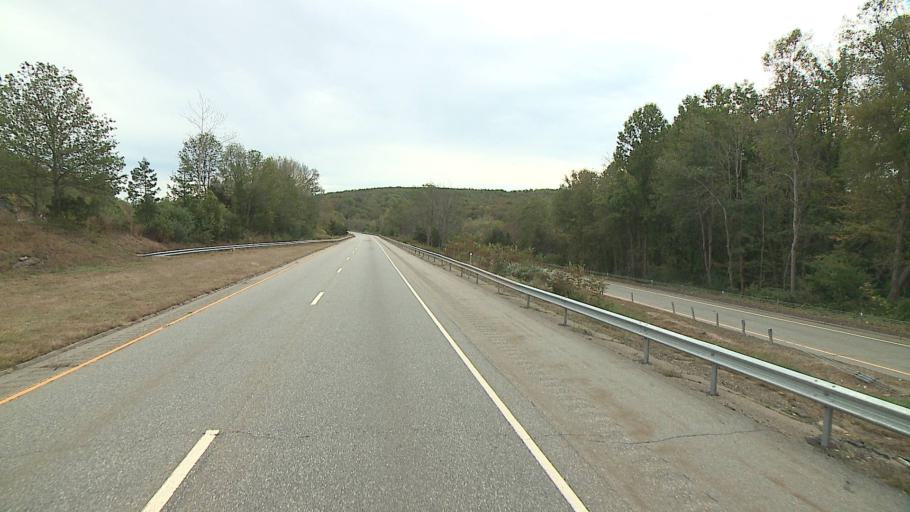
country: US
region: Connecticut
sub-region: Middlesex County
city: Chester Center
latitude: 41.4031
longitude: -72.4747
